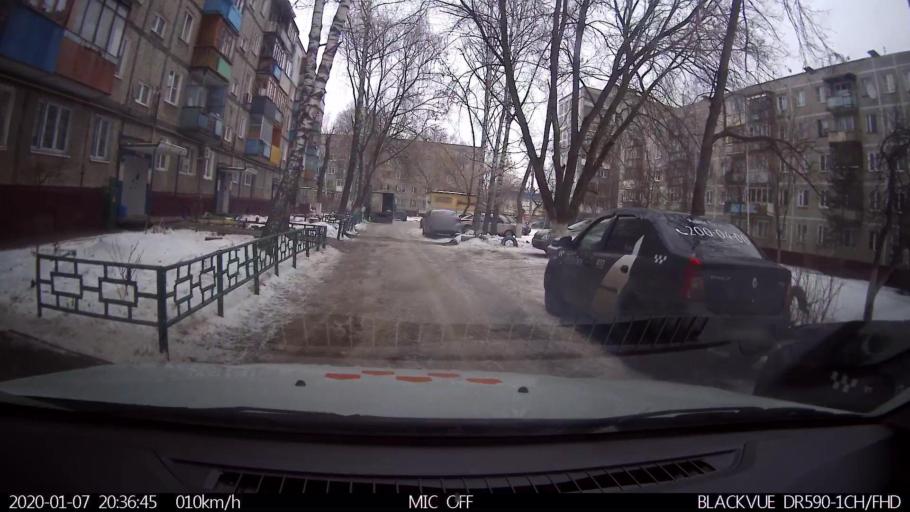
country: RU
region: Nizjnij Novgorod
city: Gorbatovka
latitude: 56.2594
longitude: 43.8784
